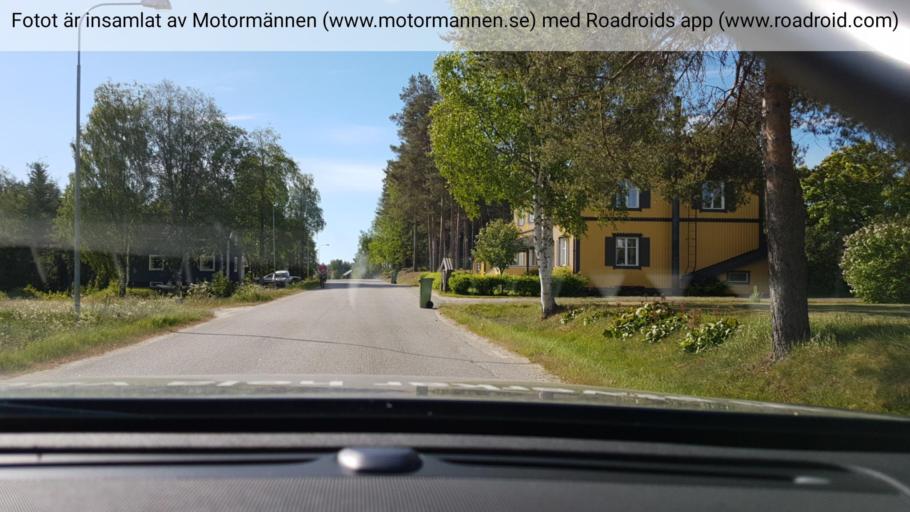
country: SE
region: Vaesterbotten
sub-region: Bjurholms Kommun
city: Bjurholm
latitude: 64.1244
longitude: 19.3043
